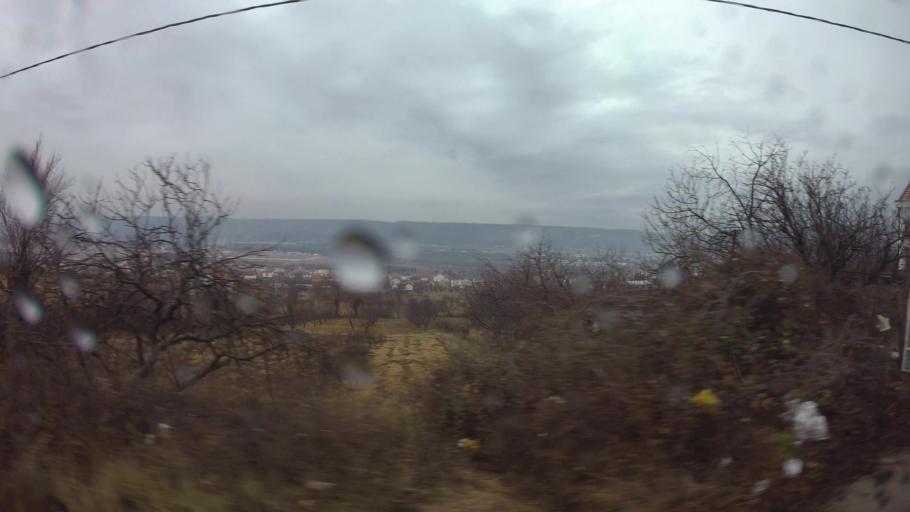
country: BA
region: Federation of Bosnia and Herzegovina
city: Rodoc
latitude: 43.3011
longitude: 17.8542
